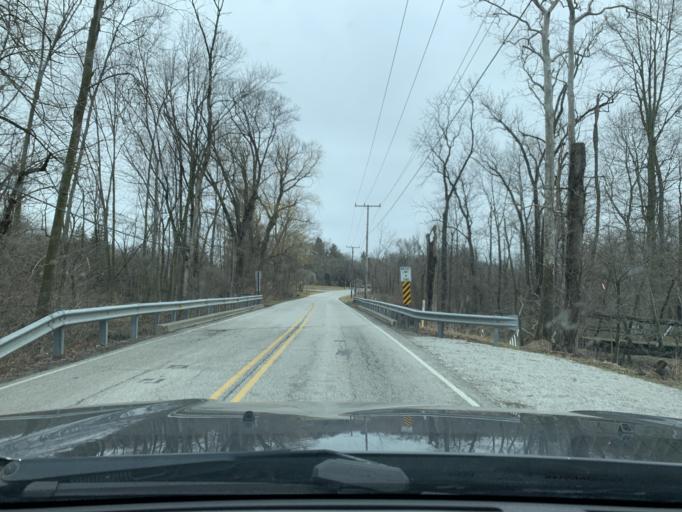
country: US
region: Indiana
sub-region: Porter County
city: Chesterton
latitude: 41.6152
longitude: -87.0166
